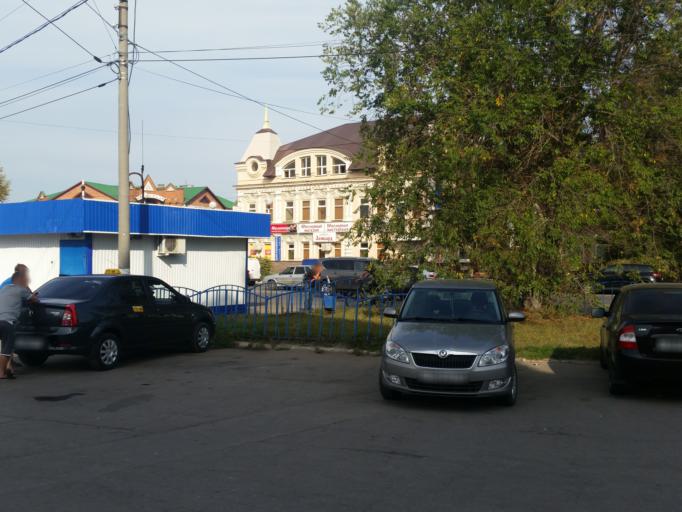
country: RU
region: Ulyanovsk
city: Dimitrovgrad
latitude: 54.2154
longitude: 49.6212
